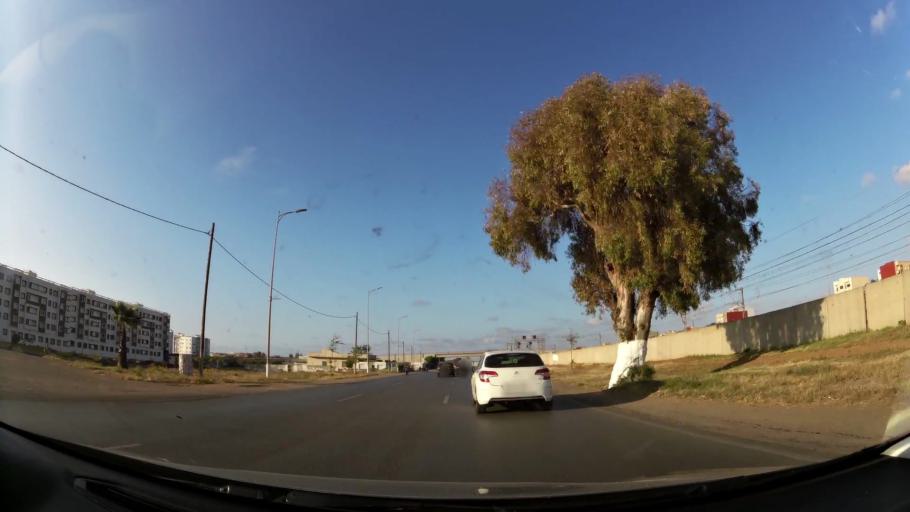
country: MA
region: Rabat-Sale-Zemmour-Zaer
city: Sale
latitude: 34.0773
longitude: -6.7809
